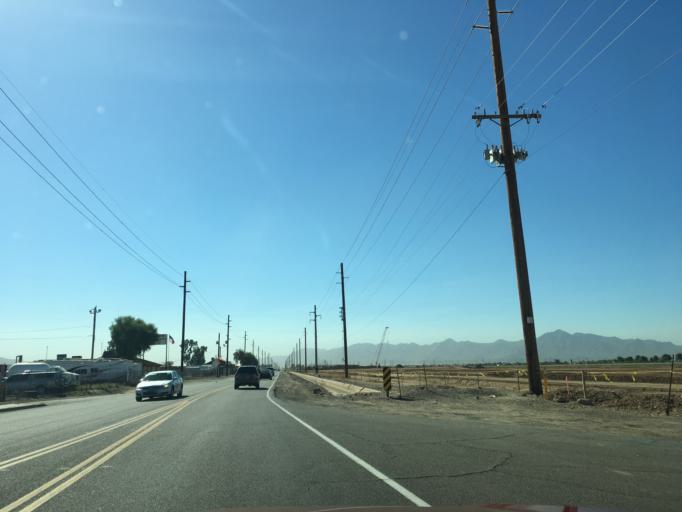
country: US
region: Arizona
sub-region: Maricopa County
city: Tolleson
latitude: 33.4366
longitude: -112.1866
